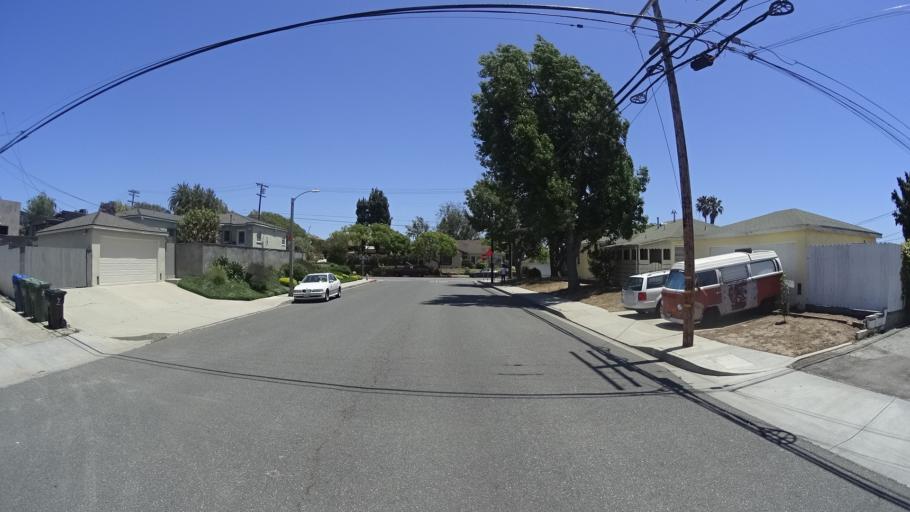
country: US
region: California
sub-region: Los Angeles County
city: Santa Monica
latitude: 34.0078
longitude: -118.4699
